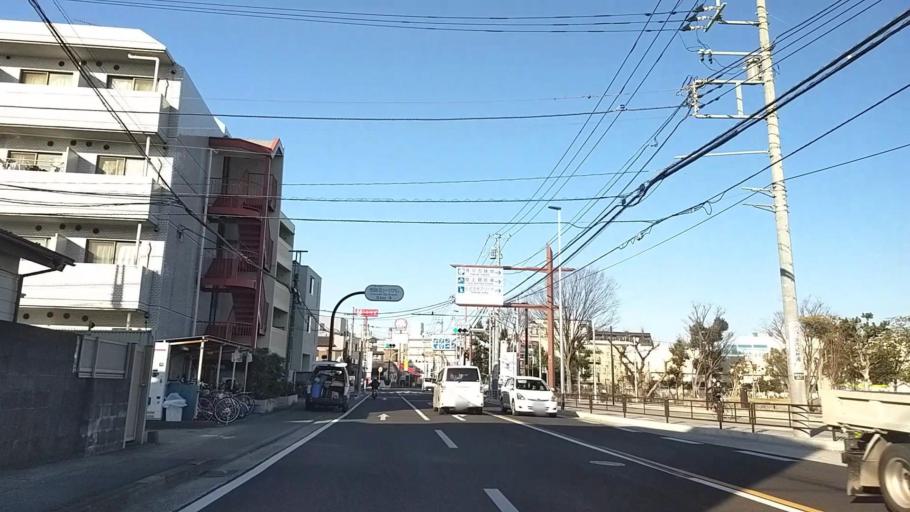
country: JP
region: Kanagawa
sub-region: Kawasaki-shi
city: Kawasaki
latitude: 35.5840
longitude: 139.6481
